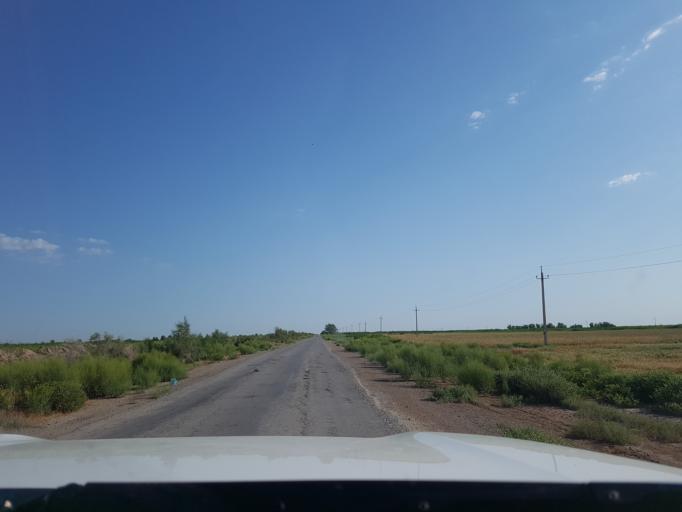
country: TM
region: Dasoguz
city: Koeneuergench
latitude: 41.9100
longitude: 58.7096
